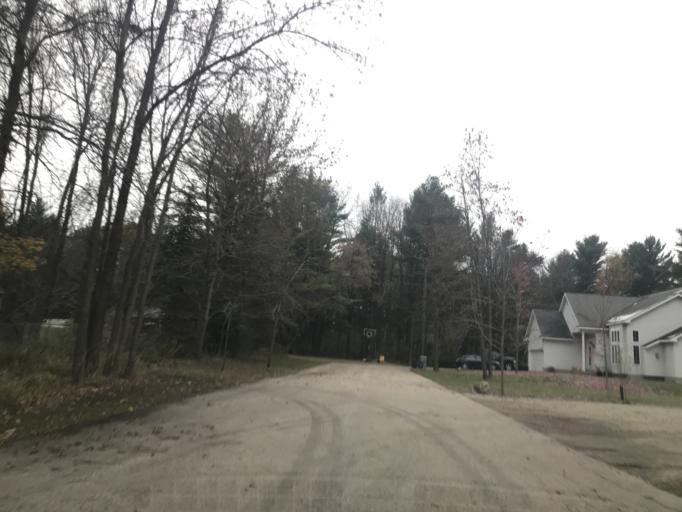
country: US
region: Wisconsin
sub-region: Marinette County
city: Marinette
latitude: 45.0942
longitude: -87.6547
